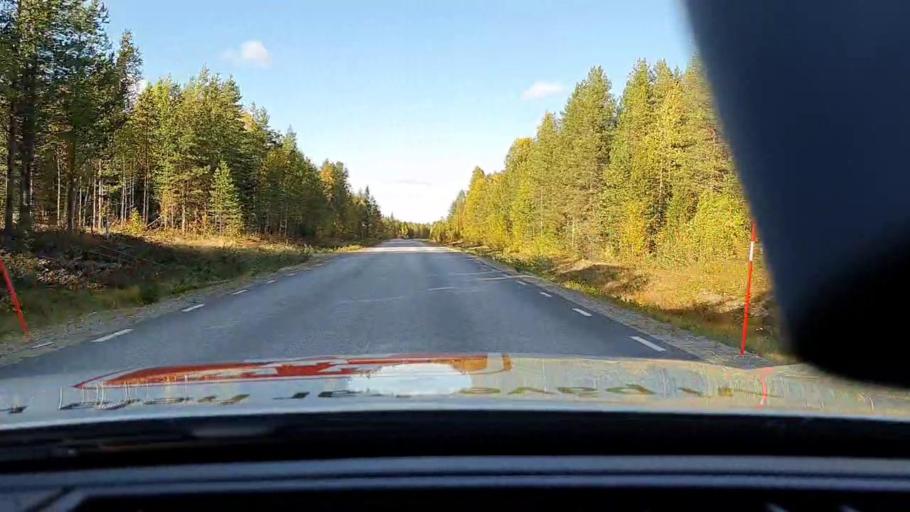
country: SE
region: Norrbotten
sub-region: Pitea Kommun
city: Norrfjarden
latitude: 65.4971
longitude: 21.4753
